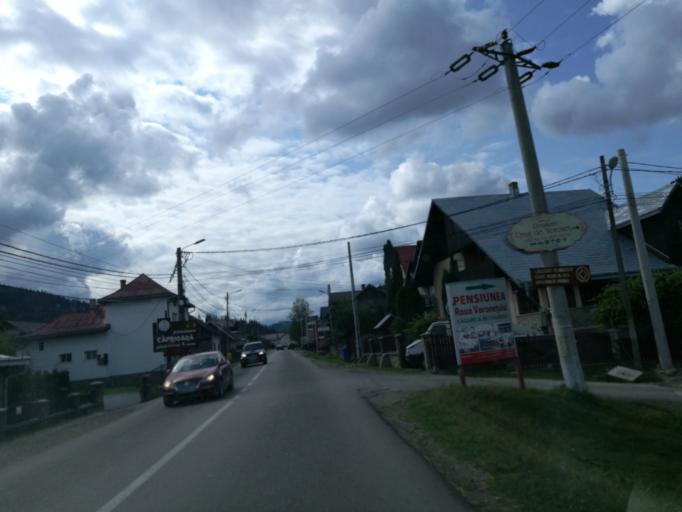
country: RO
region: Suceava
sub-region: Oras Gura Humorului
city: Gura Humorului
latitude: 47.5373
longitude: 25.8644
